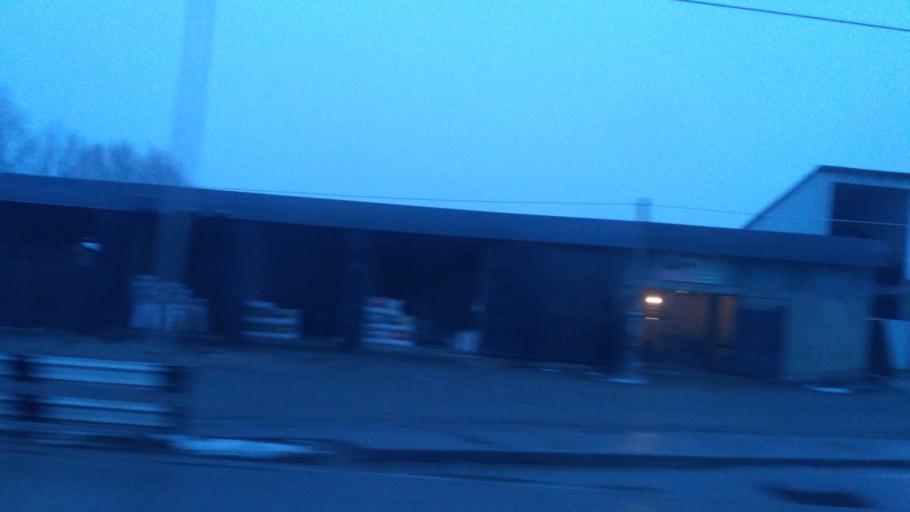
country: KZ
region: Ongtustik Qazaqstan
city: Shymkent
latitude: 42.3661
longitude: 69.5141
